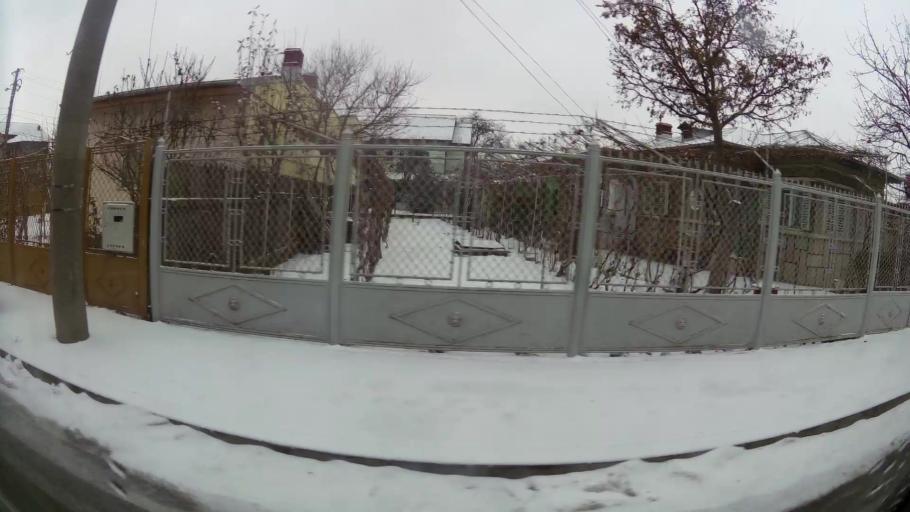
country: RO
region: Prahova
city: Ploiesti
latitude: 44.9279
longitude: 26.0202
